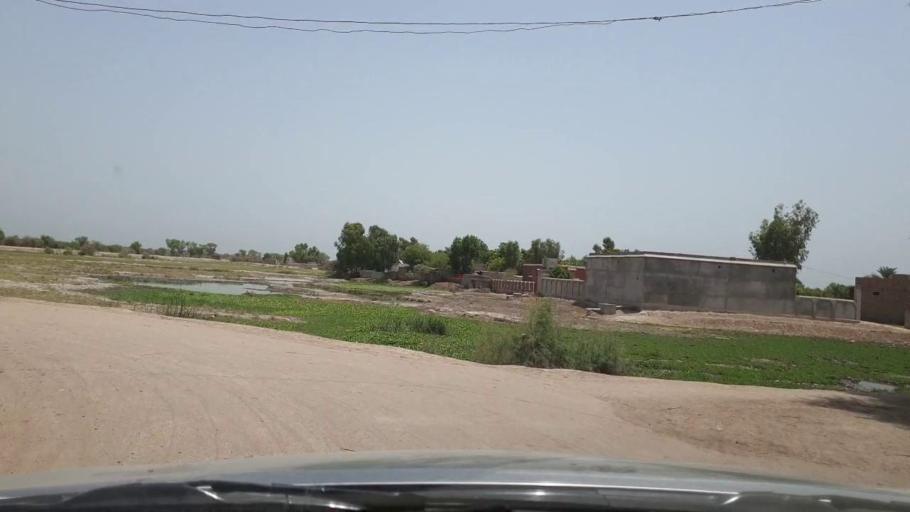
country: PK
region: Sindh
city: Pano Aqil
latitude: 27.8748
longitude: 69.1541
